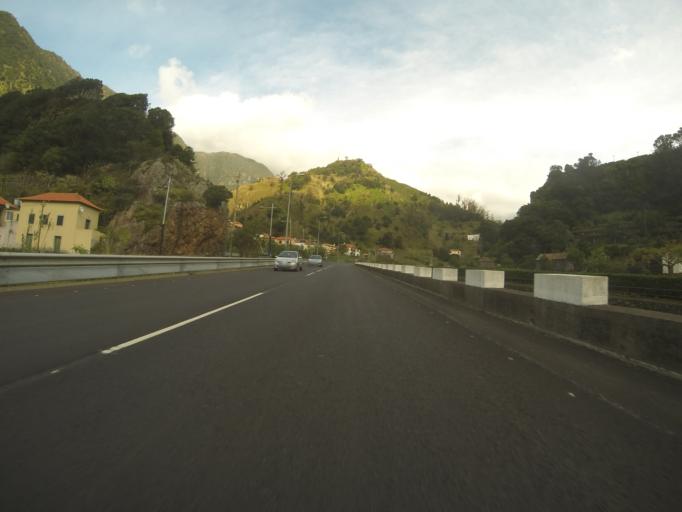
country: PT
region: Madeira
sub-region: Sao Vicente
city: Sao Vicente
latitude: 32.7978
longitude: -17.0416
